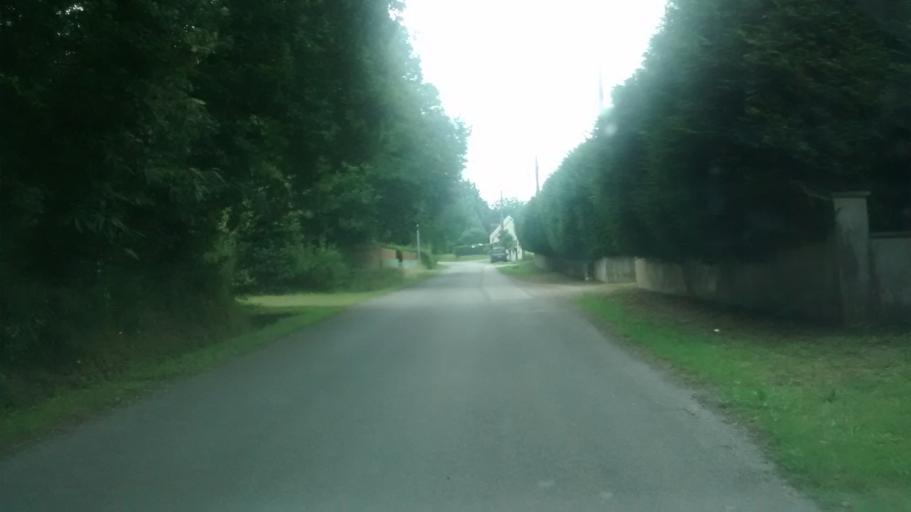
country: FR
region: Brittany
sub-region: Departement du Morbihan
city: Molac
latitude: 47.7837
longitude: -2.4379
